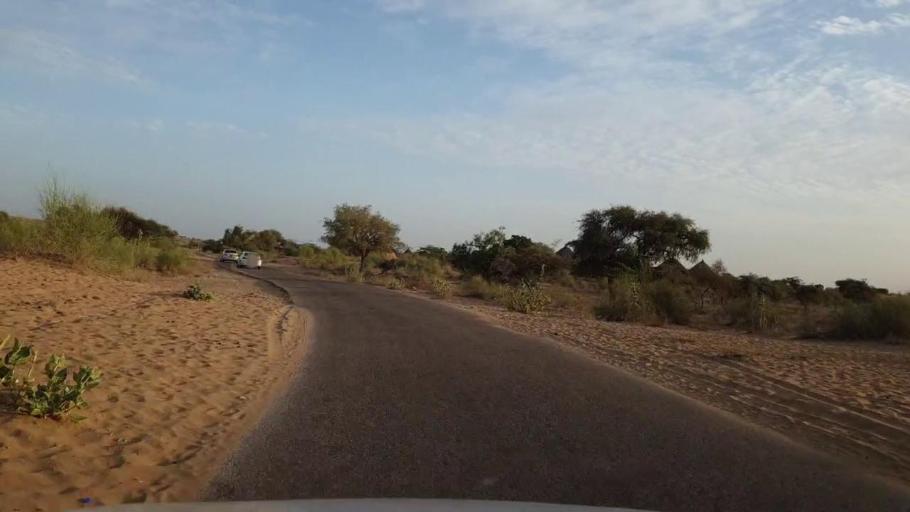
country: PK
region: Sindh
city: Nabisar
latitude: 25.0588
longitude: 69.9649
